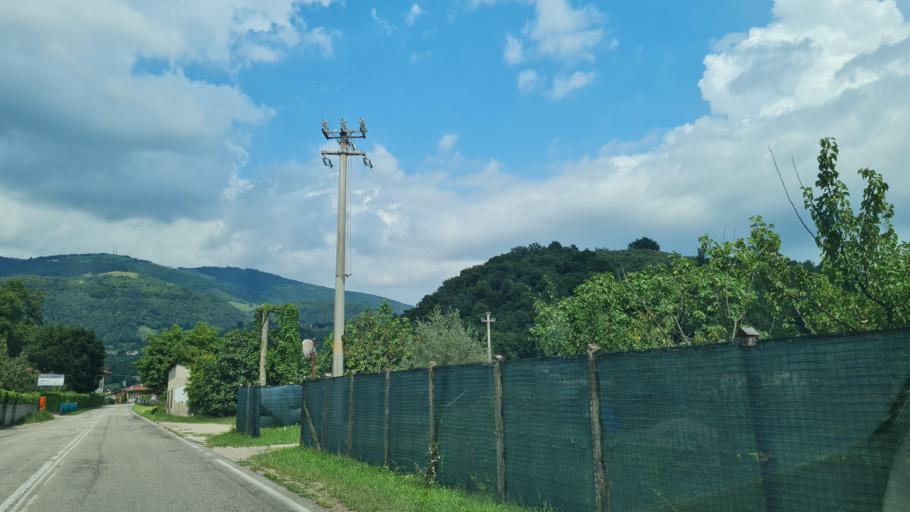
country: IT
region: Veneto
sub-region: Provincia di Vicenza
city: Marostica
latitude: 45.7600
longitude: 11.6608
